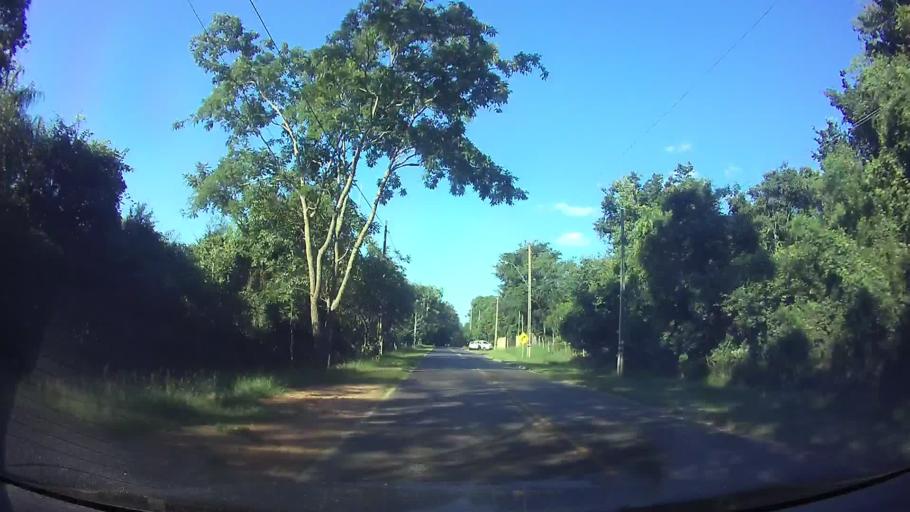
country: PY
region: Cordillera
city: Atyra
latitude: -25.2915
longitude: -57.1818
